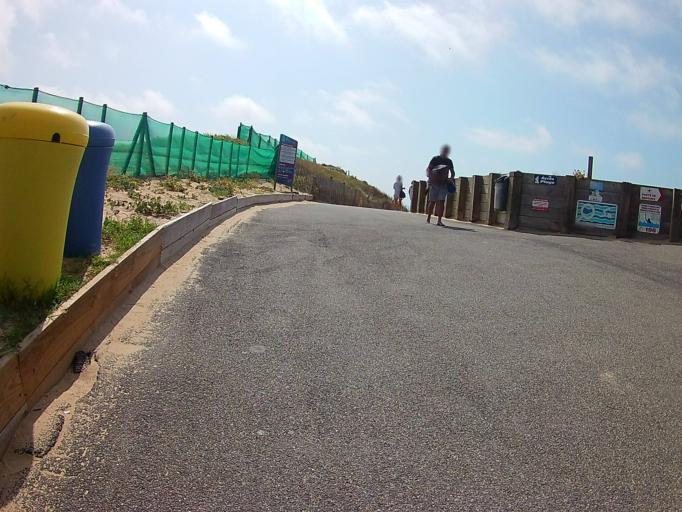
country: FR
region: Aquitaine
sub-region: Departement des Landes
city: Ondres
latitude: 43.5994
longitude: -1.4725
